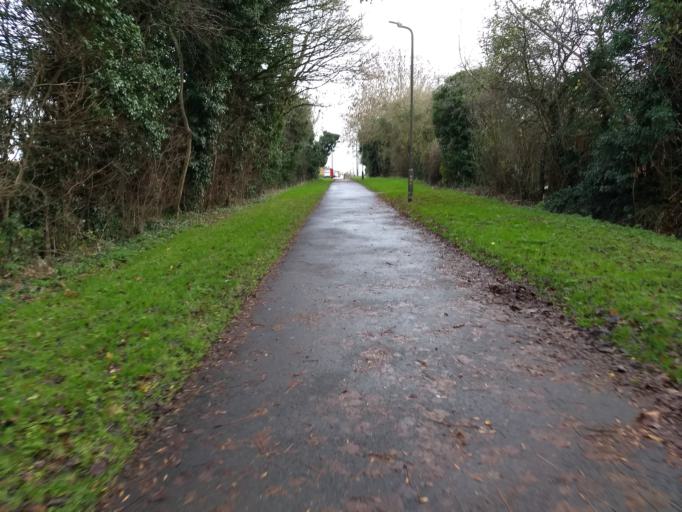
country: GB
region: England
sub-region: Buckinghamshire
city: Newton Longville
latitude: 51.9952
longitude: -0.7666
